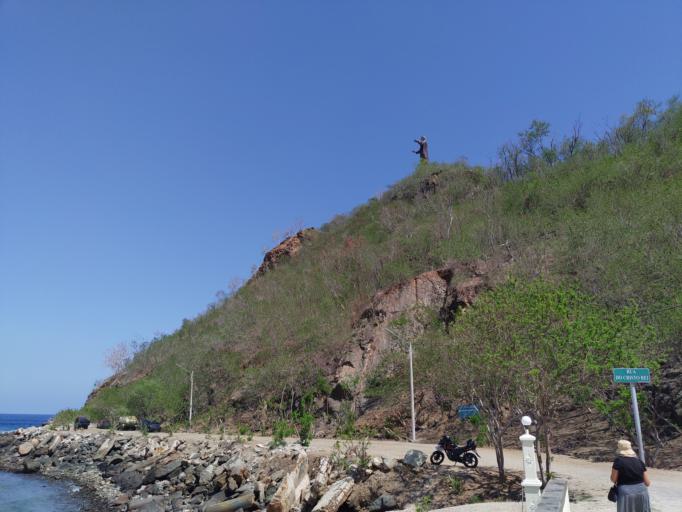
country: TL
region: Dili
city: Dili
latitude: -8.5223
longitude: 125.6092
